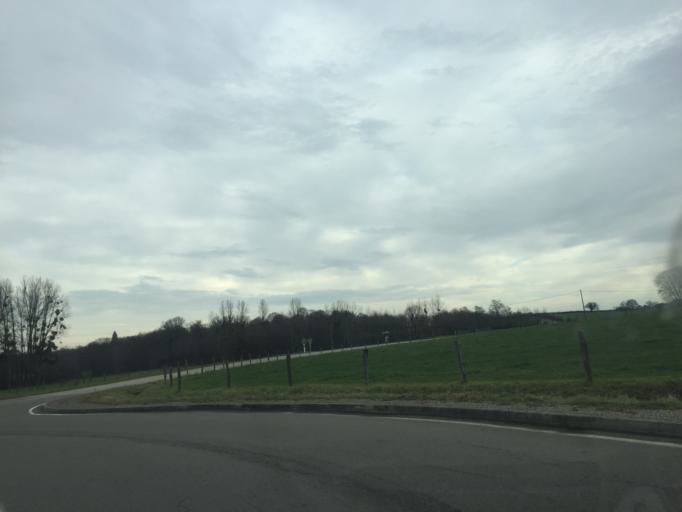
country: FR
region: Franche-Comte
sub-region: Departement du Jura
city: Poligny
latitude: 46.8497
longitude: 5.5787
